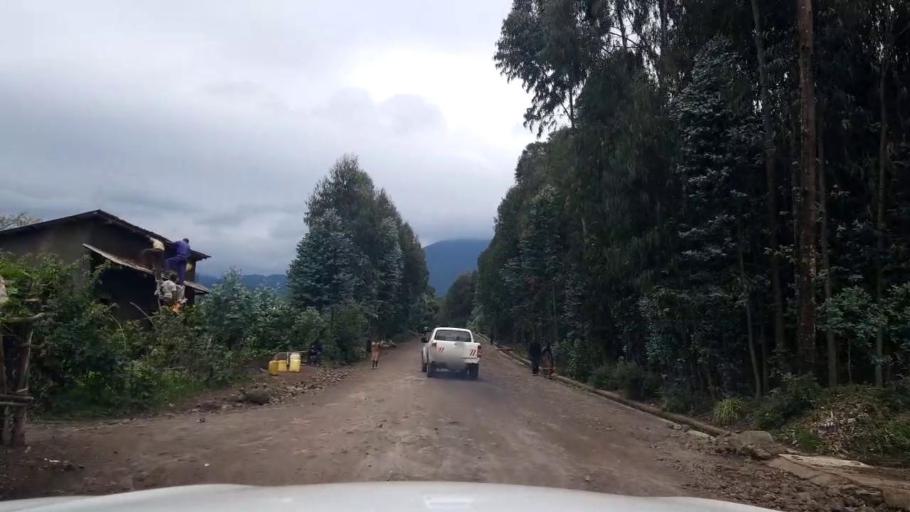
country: RW
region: Northern Province
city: Musanze
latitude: -1.4441
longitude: 29.5342
